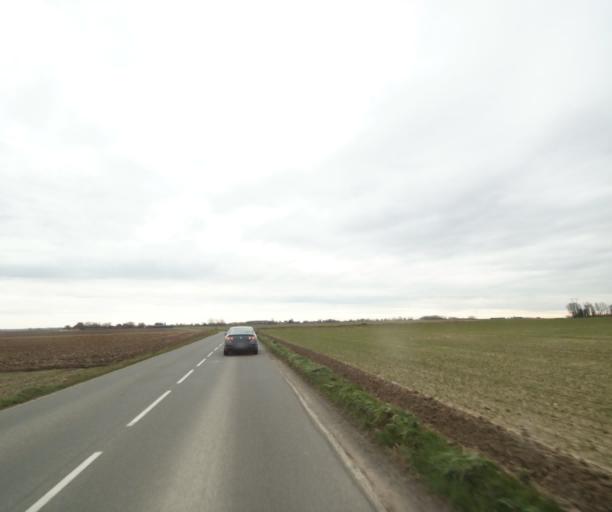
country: FR
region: Nord-Pas-de-Calais
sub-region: Departement du Nord
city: Sebourg
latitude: 50.3532
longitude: 3.6197
